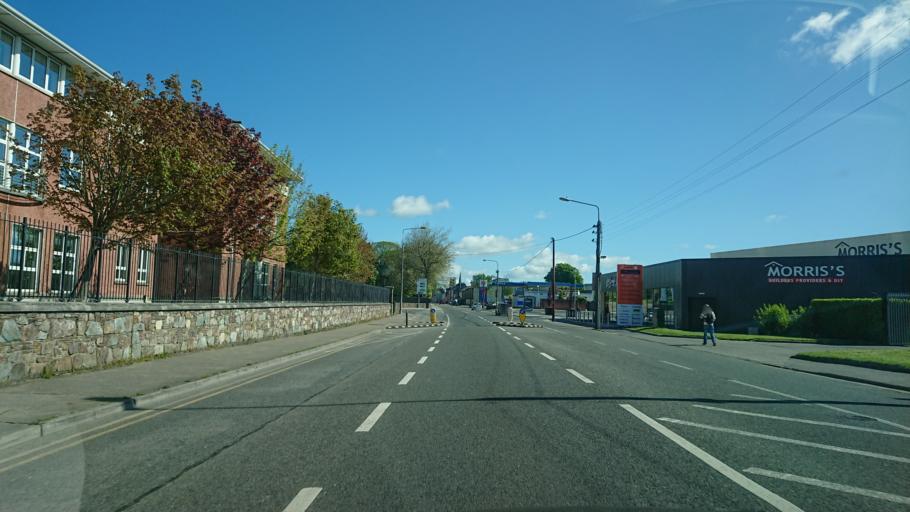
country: IE
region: Munster
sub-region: Waterford
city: Waterford
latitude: 52.2521
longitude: -7.1167
